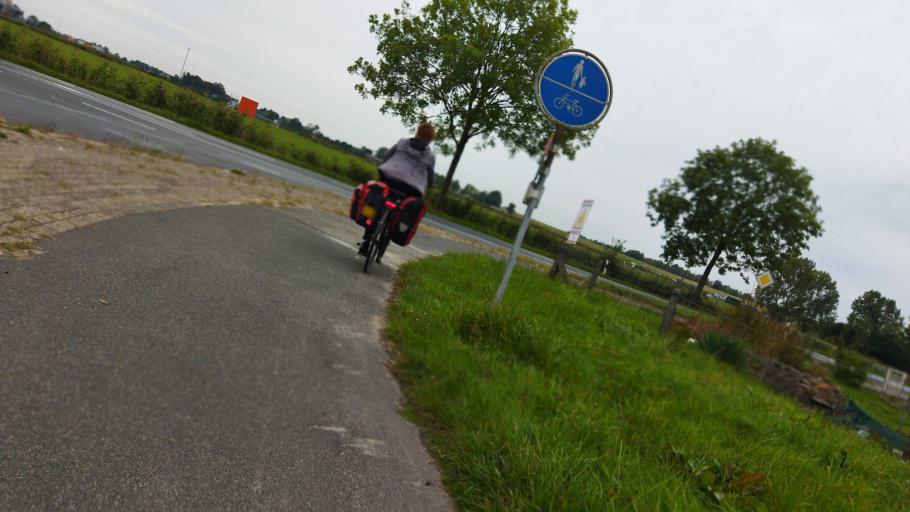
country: DE
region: Lower Saxony
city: Jemgum
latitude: 53.2621
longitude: 7.4124
